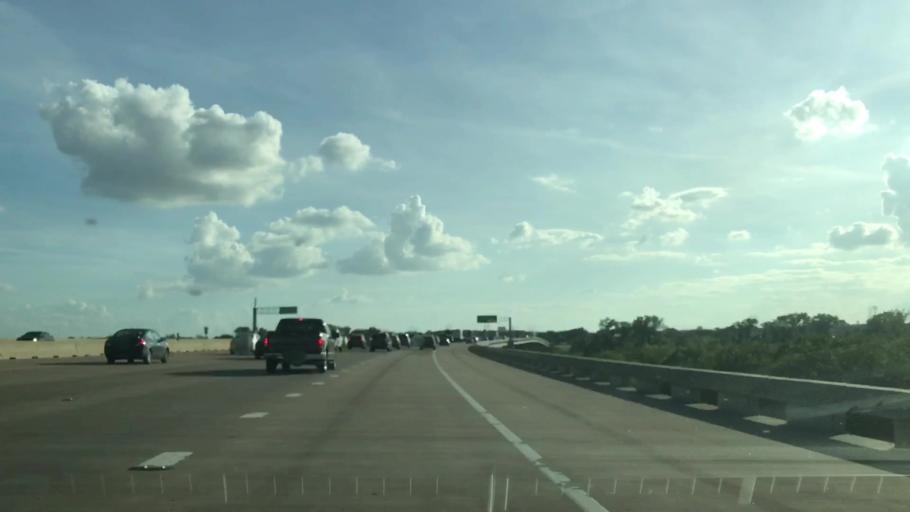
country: US
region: Texas
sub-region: Dallas County
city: Grand Prairie
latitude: 32.7841
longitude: -97.0214
